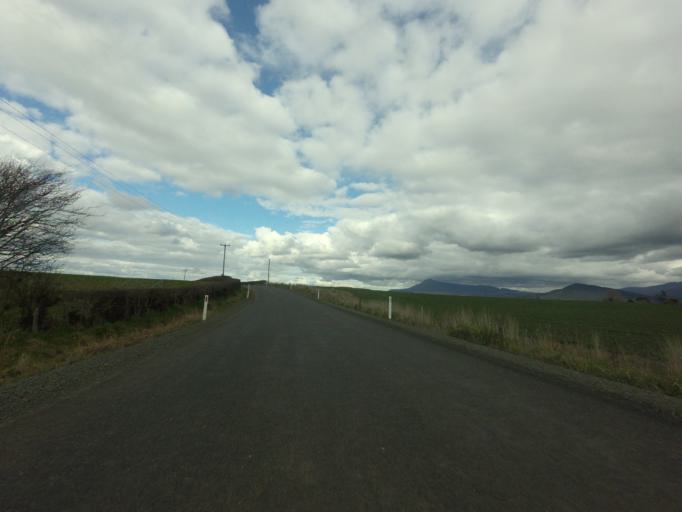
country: AU
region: Tasmania
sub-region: Northern Midlands
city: Longford
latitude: -41.7840
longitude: 147.0984
